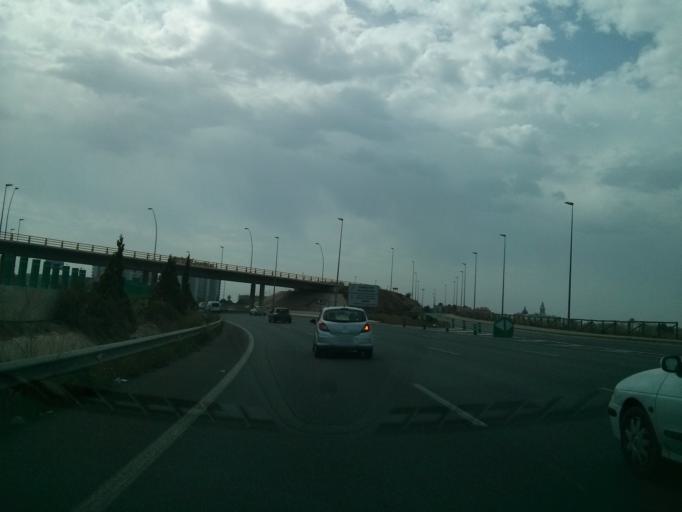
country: ES
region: Valencia
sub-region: Provincia de Valencia
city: Burjassot
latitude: 39.5031
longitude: -0.3935
